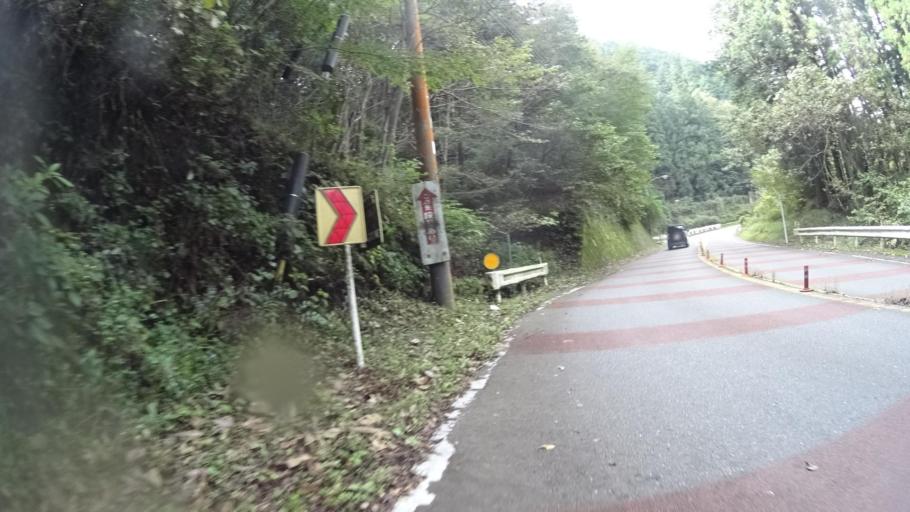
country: JP
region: Yamanashi
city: Uenohara
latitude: 35.7009
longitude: 139.1116
